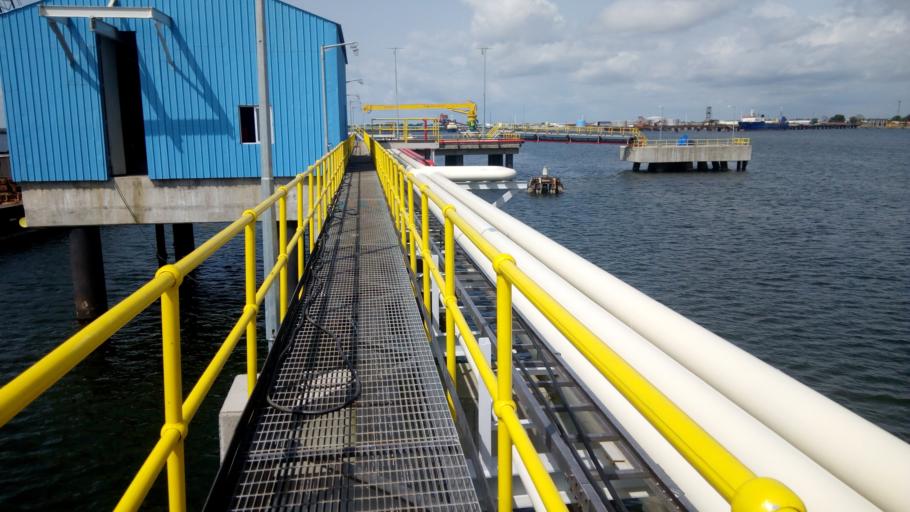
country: LR
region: Montserrado
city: Monrovia
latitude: 6.3421
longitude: -10.8025
